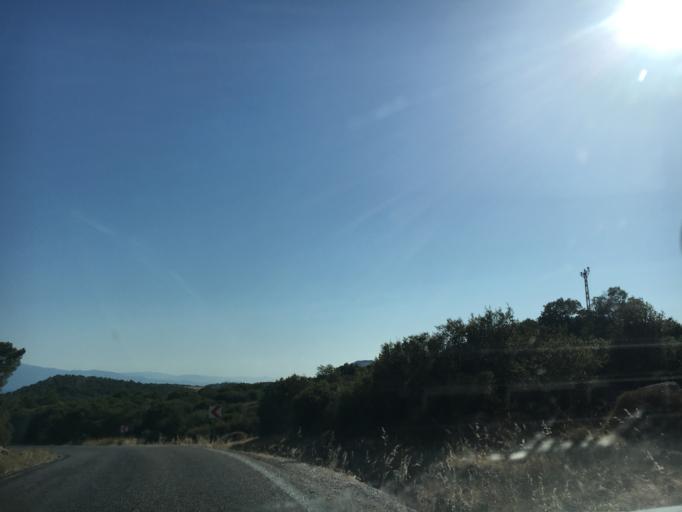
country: TR
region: Canakkale
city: Behram
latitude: 39.5041
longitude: 26.3670
